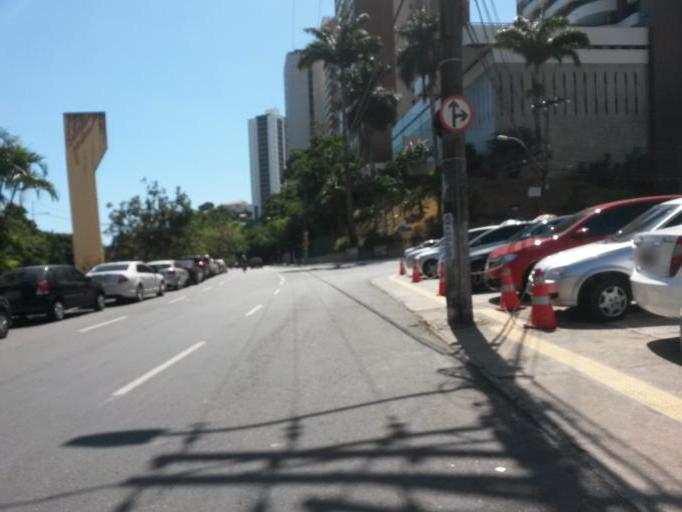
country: BR
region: Bahia
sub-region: Salvador
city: Salvador
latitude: -12.9959
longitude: -38.4776
